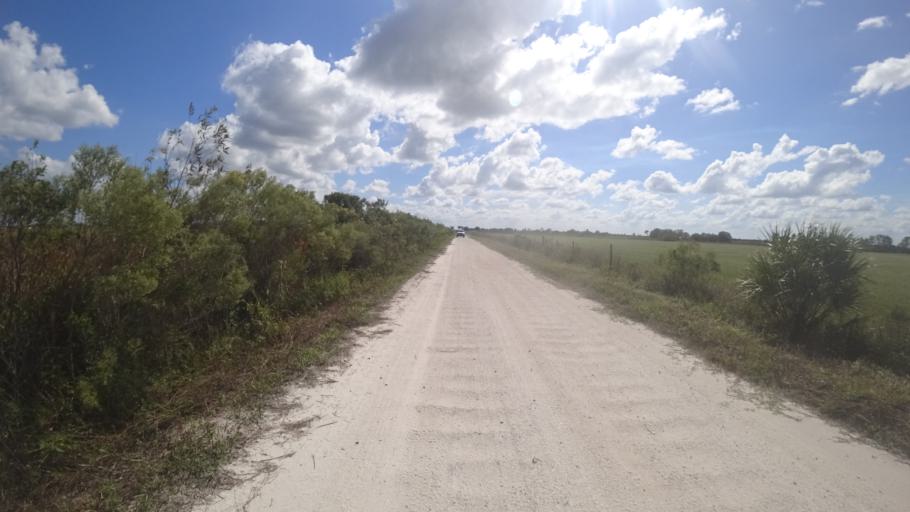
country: US
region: Florida
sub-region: DeSoto County
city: Arcadia
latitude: 27.3170
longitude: -82.1051
